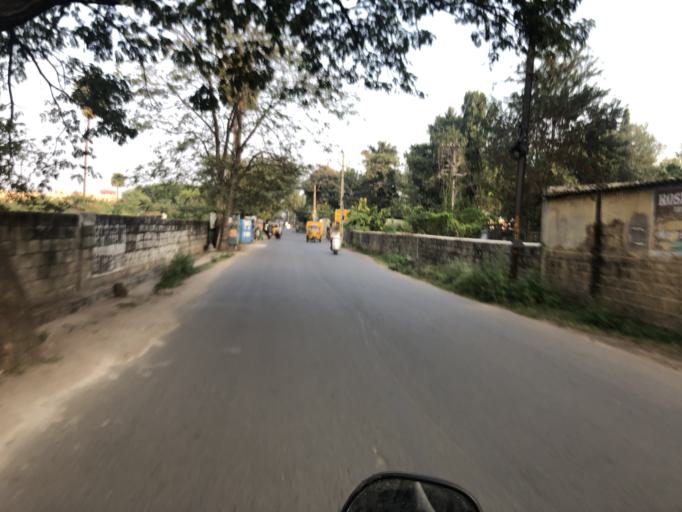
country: IN
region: Telangana
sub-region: Rangareddi
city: Kukatpalli
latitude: 17.4627
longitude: 78.4358
